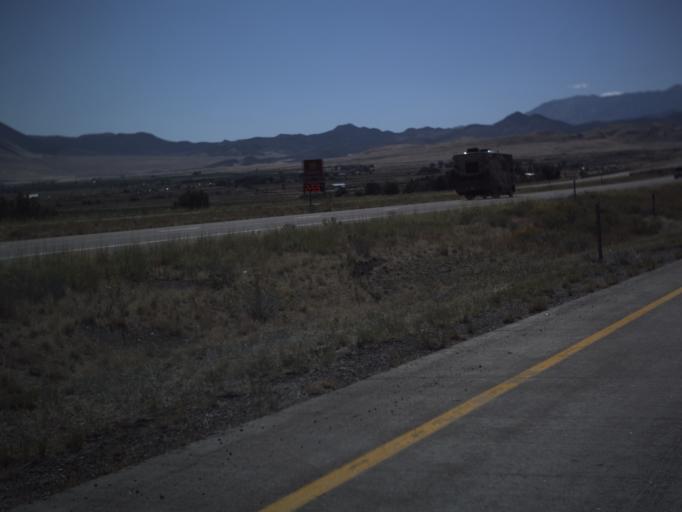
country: US
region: Utah
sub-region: Sevier County
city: Monroe
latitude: 38.6864
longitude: -112.1543
